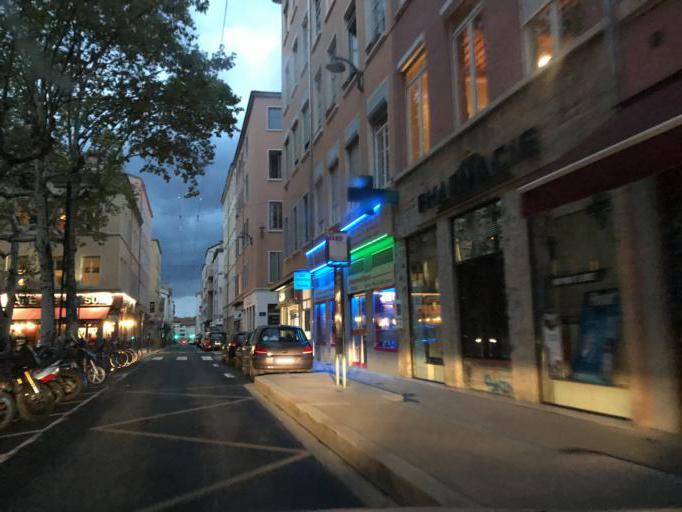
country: FR
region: Rhone-Alpes
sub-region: Departement du Rhone
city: Caluire-et-Cuire
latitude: 45.7775
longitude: 4.8349
